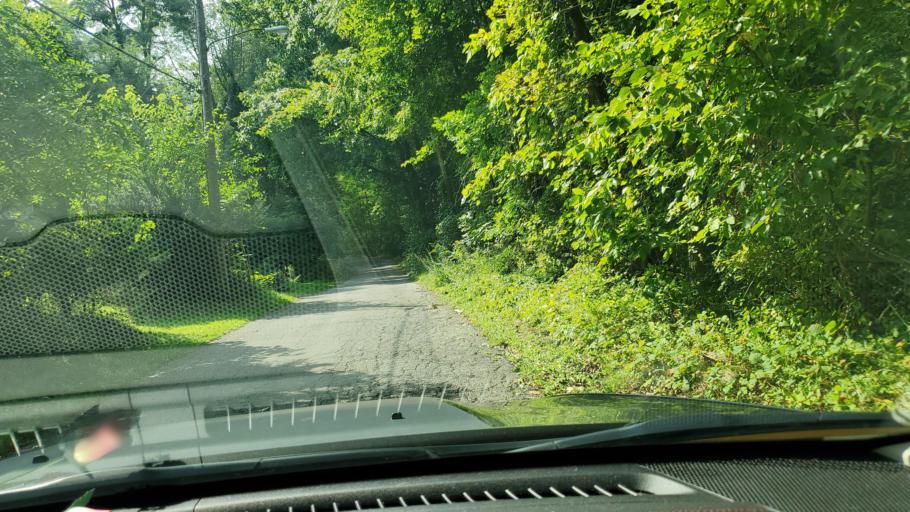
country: US
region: Ohio
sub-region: Mahoning County
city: Struthers
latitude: 41.0497
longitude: -80.5882
